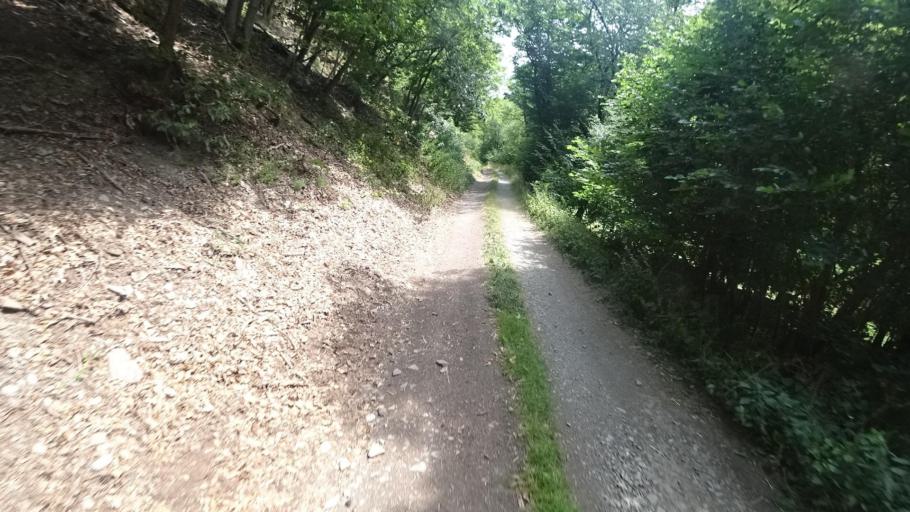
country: DE
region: Rheinland-Pfalz
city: Heckenbach
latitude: 50.4814
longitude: 7.0678
